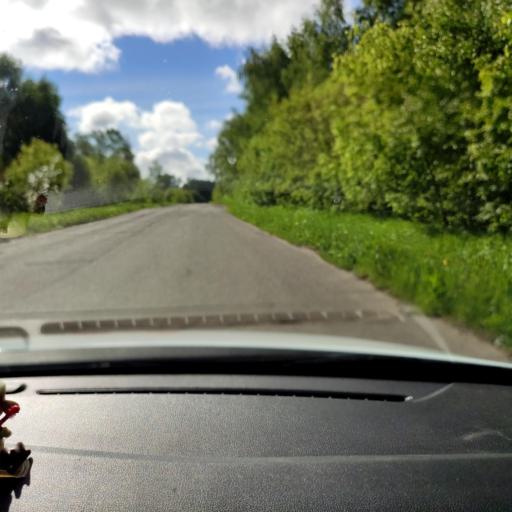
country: RU
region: Tatarstan
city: Stolbishchi
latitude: 55.7183
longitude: 49.2163
